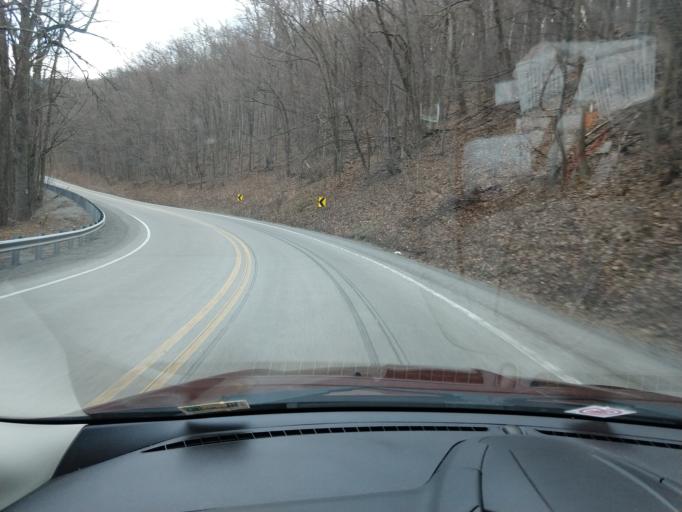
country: US
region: West Virginia
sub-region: Randolph County
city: Elkins
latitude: 38.6601
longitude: -79.9215
